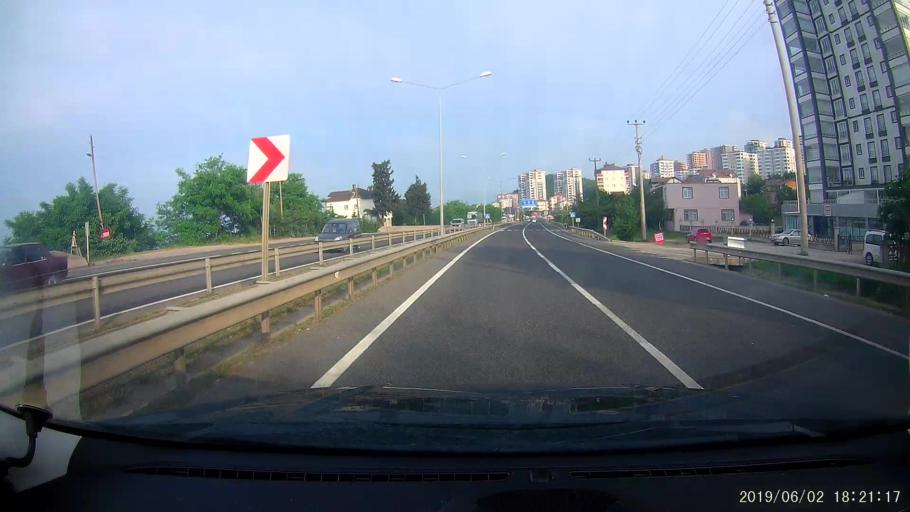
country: TR
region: Ordu
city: Fatsa
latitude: 41.0668
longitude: 37.4670
